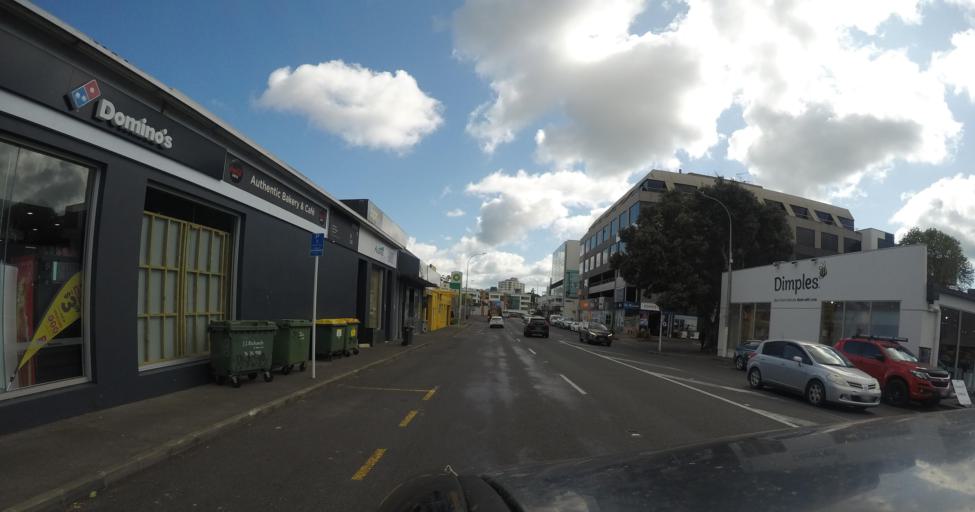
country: NZ
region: Auckland
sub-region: Auckland
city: Auckland
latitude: -36.8680
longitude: 174.7751
